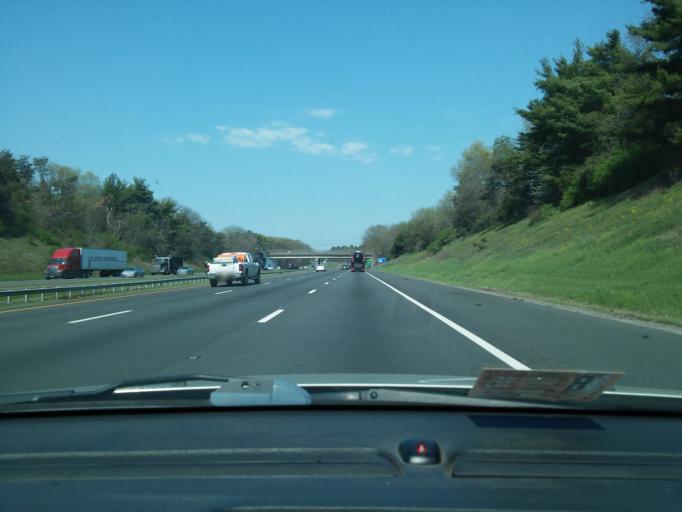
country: US
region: New Jersey
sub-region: Hunterdon County
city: Whitehouse Station
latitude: 40.6488
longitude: -74.7380
